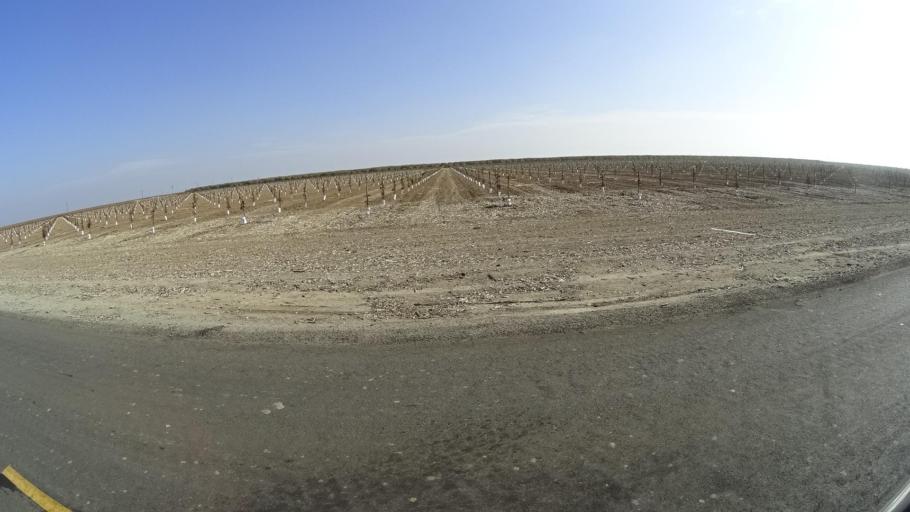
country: US
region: California
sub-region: Kern County
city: McFarland
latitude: 35.6794
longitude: -119.1693
